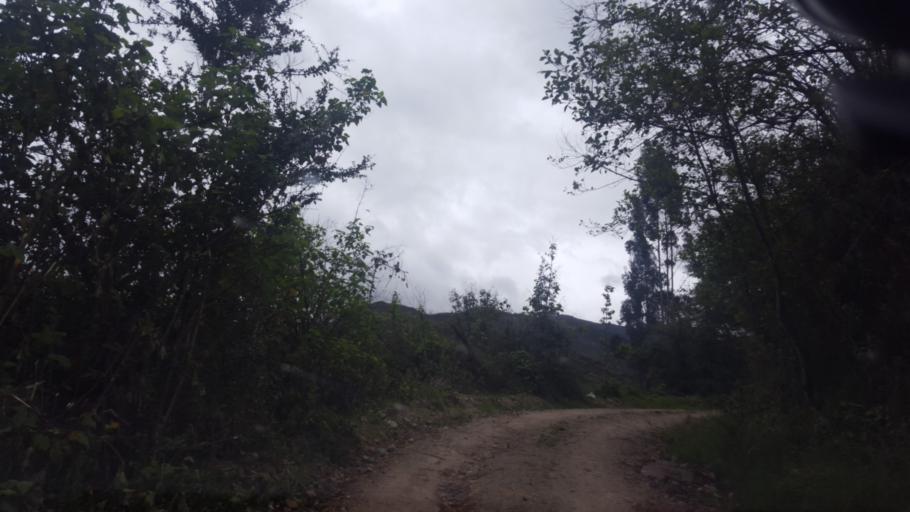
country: CO
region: Boyaca
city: Socha Viejo
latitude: 6.0113
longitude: -72.8041
